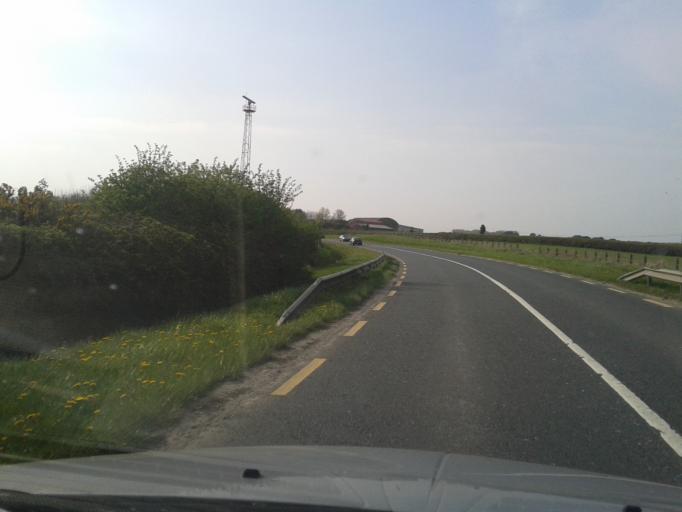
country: IE
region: Leinster
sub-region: Fingal County
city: Swords
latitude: 53.4386
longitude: -6.2543
